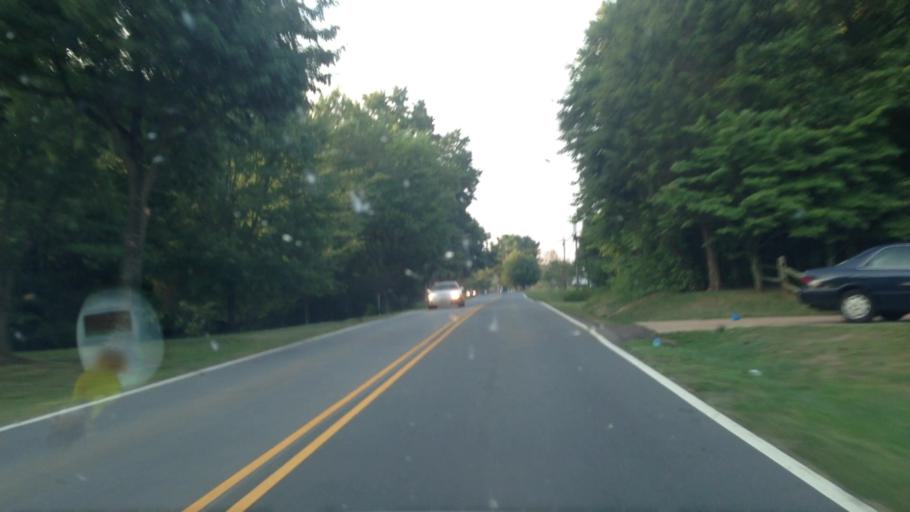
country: US
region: North Carolina
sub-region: Forsyth County
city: Kernersville
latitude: 36.1493
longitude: -80.0891
